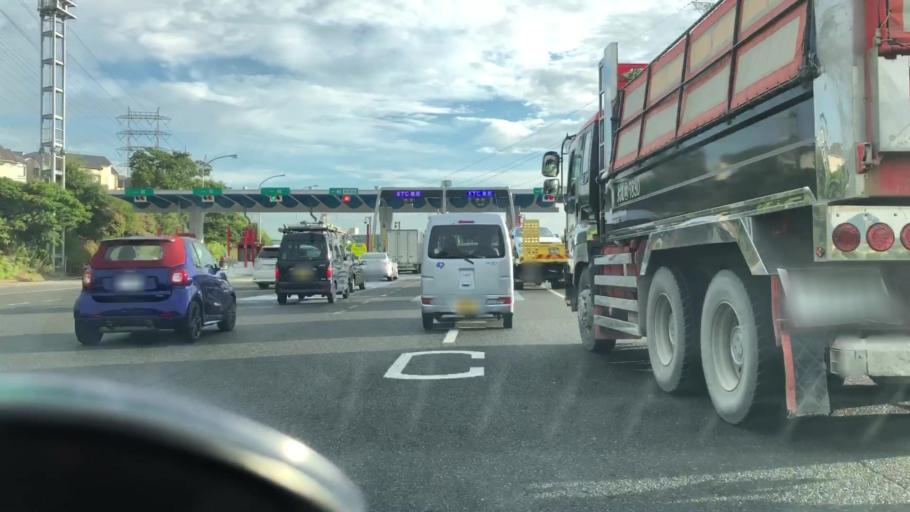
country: JP
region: Hyogo
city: Takarazuka
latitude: 34.8057
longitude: 135.3686
